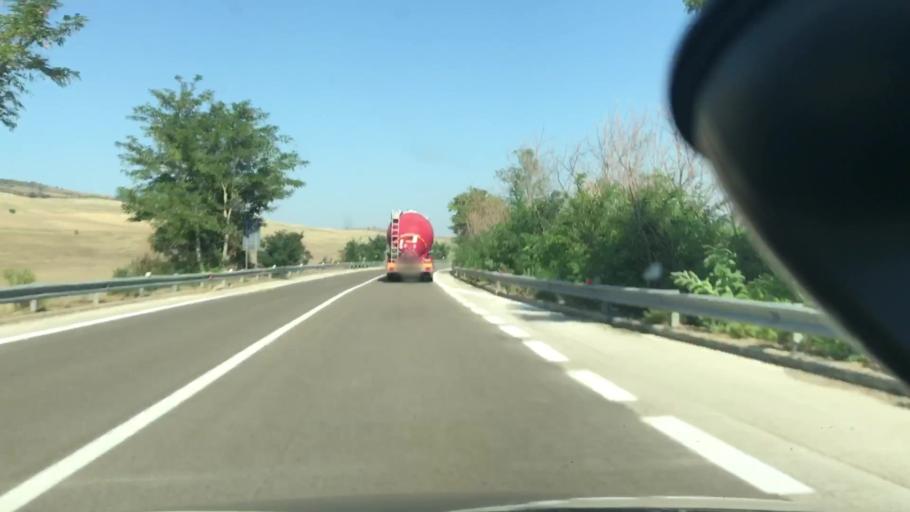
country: IT
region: Basilicate
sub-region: Provincia di Matera
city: Irsina
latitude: 40.7936
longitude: 16.2788
